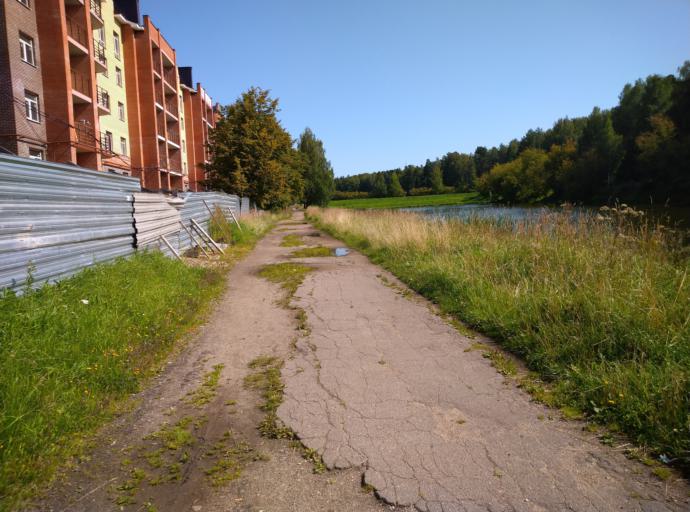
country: RU
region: Kostroma
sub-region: Kostromskoy Rayon
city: Kostroma
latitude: 57.7979
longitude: 40.9563
